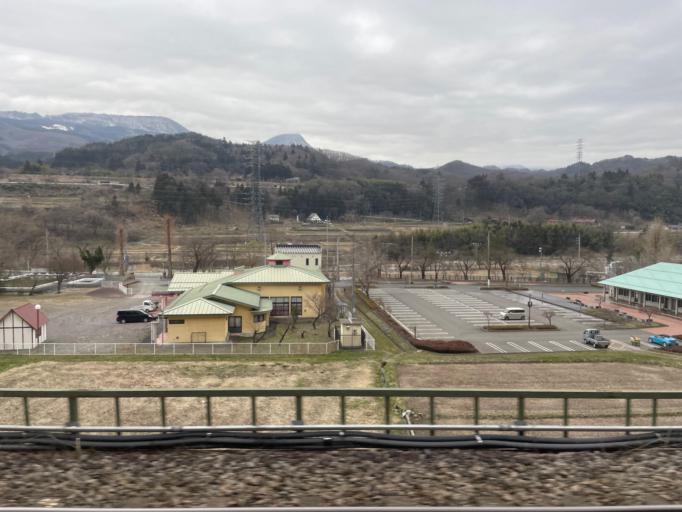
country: JP
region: Gunma
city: Numata
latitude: 36.7296
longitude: 138.9832
